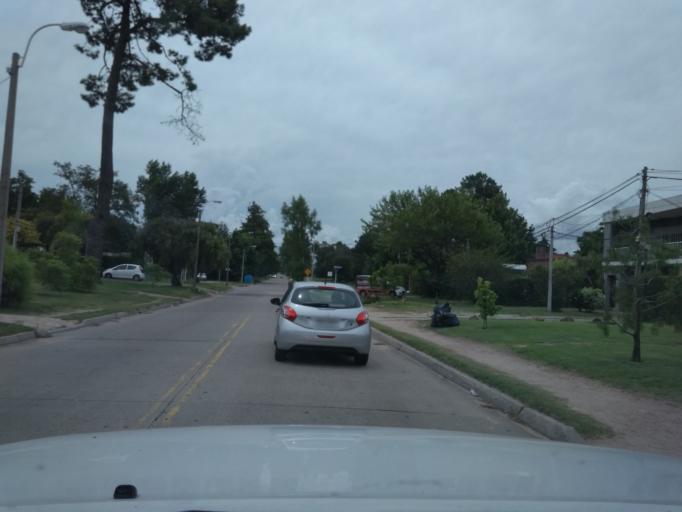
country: UY
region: Canelones
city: Paso de Carrasco
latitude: -34.8766
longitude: -56.0580
